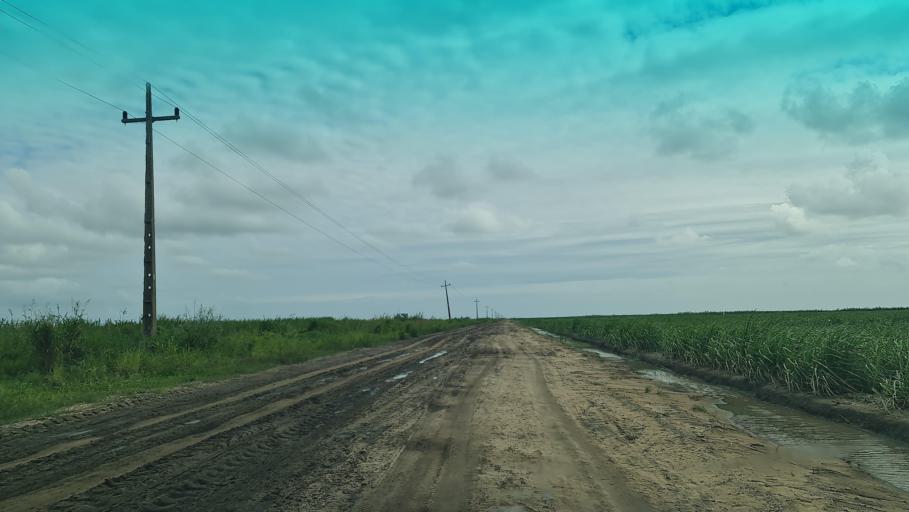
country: MZ
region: Maputo
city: Manhica
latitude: -25.4465
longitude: 32.8396
